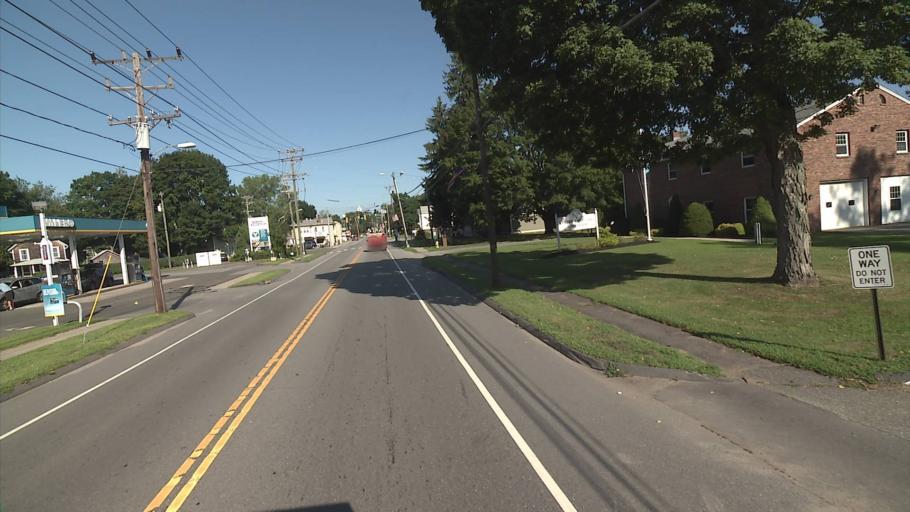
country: US
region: Connecticut
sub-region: Middlesex County
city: Westbrook Center
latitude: 41.2841
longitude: -72.4445
